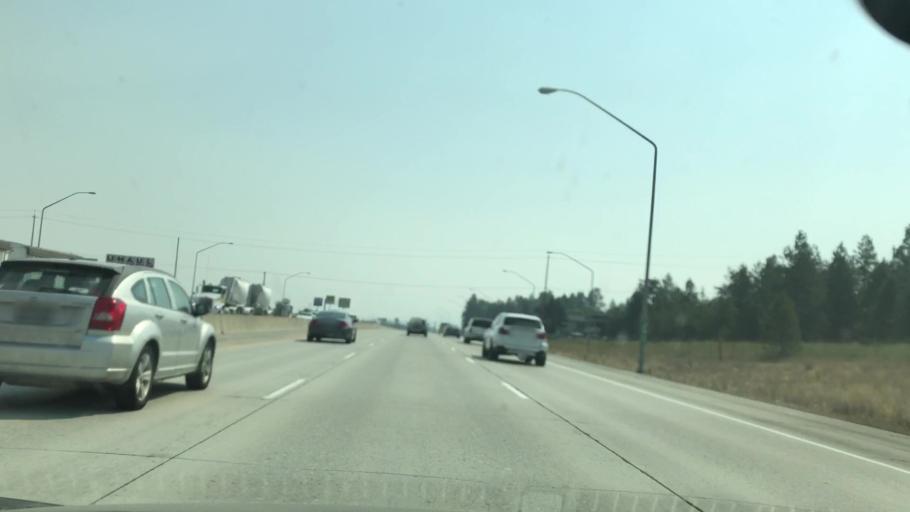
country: US
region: Washington
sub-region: Spokane County
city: Spokane Valley
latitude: 47.6739
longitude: -117.2374
